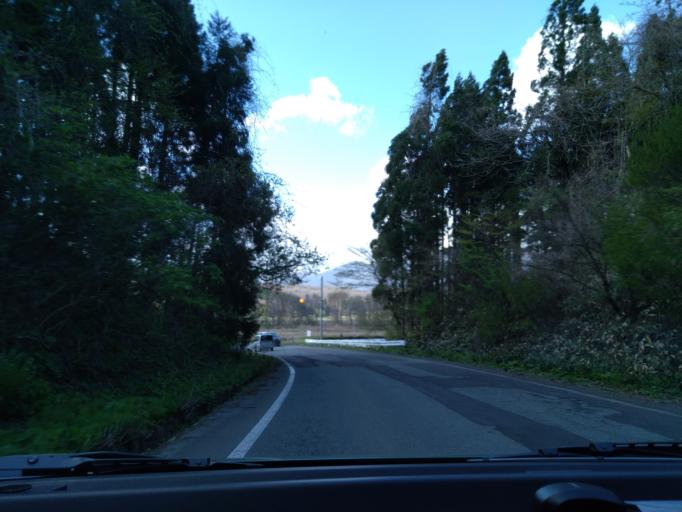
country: JP
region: Akita
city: Akita
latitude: 39.6920
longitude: 140.2747
